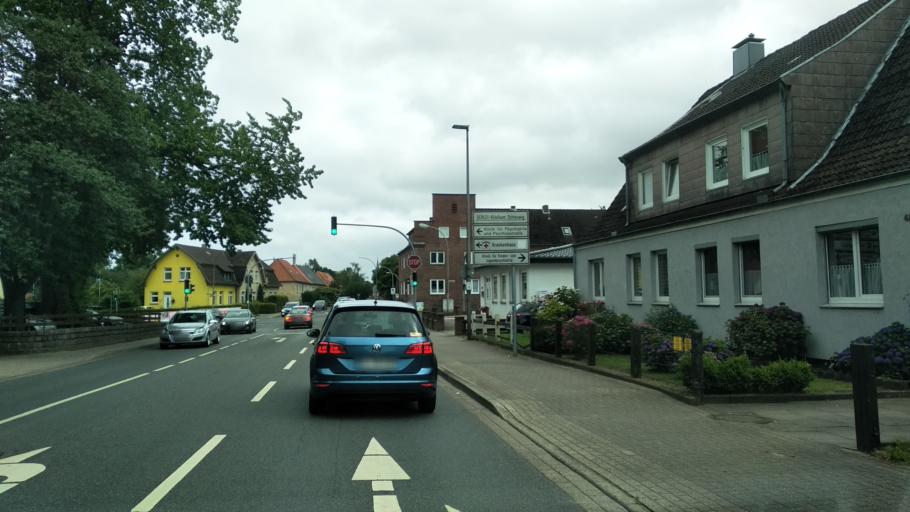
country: DE
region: Schleswig-Holstein
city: Schleswig
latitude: 54.5255
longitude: 9.5604
